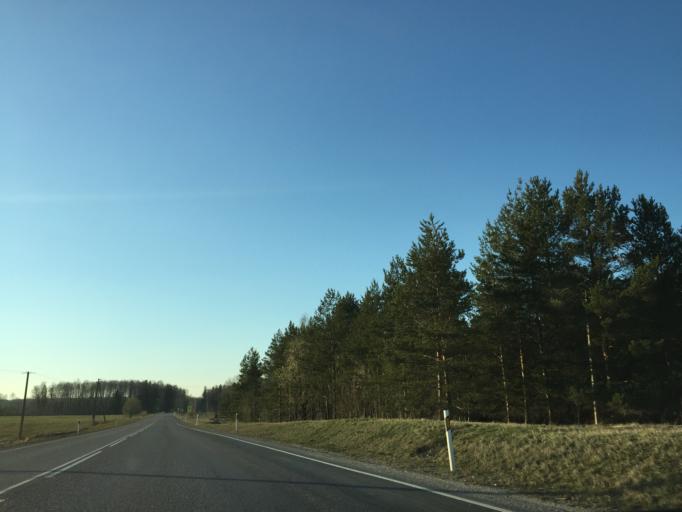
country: EE
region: Ida-Virumaa
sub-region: Johvi vald
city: Johvi
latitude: 59.3163
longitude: 27.4954
